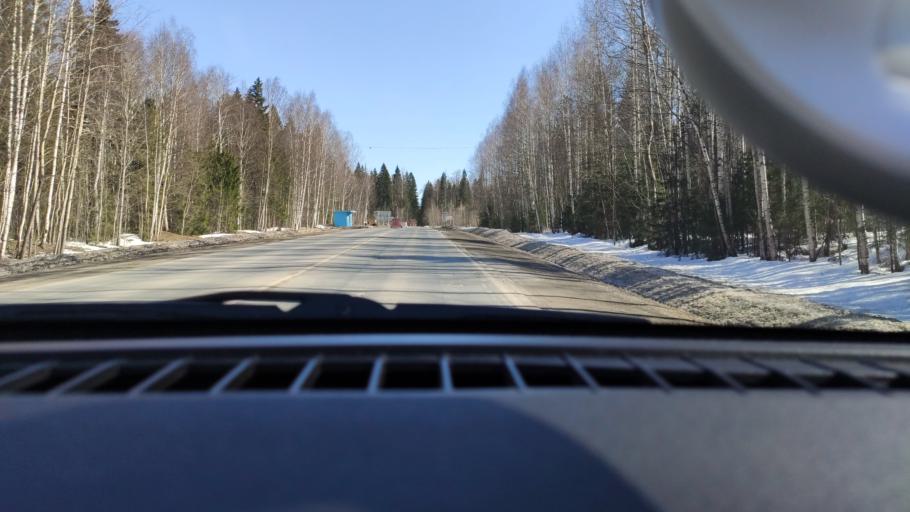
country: RU
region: Perm
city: Perm
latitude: 58.1355
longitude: 56.2990
